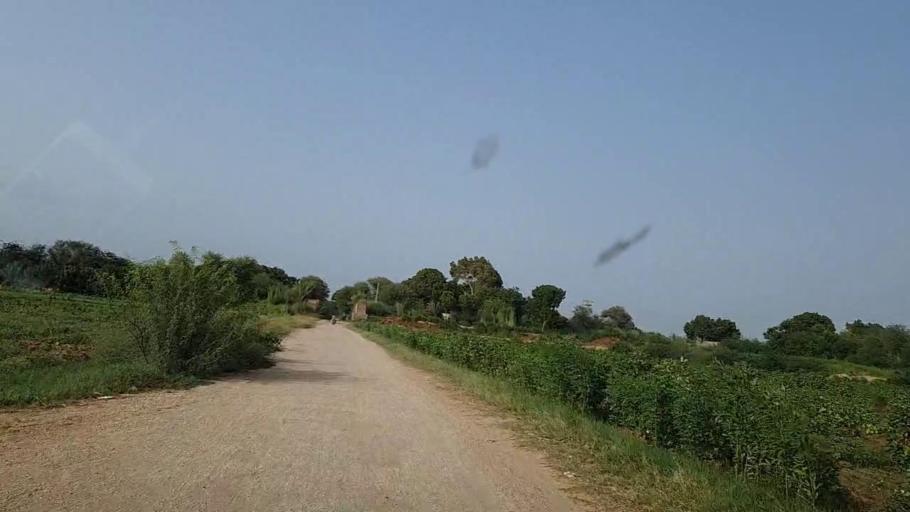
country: PK
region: Sindh
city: Kotri
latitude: 25.2343
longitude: 68.2609
